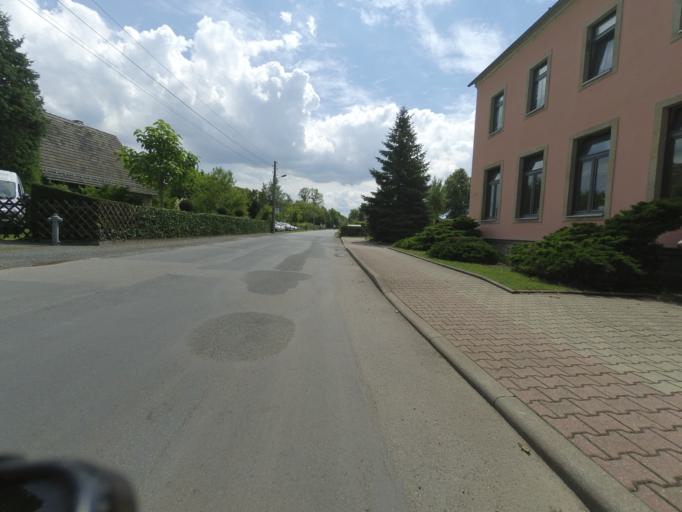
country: DE
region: Saxony
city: Heidenau
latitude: 50.9785
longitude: 13.8881
